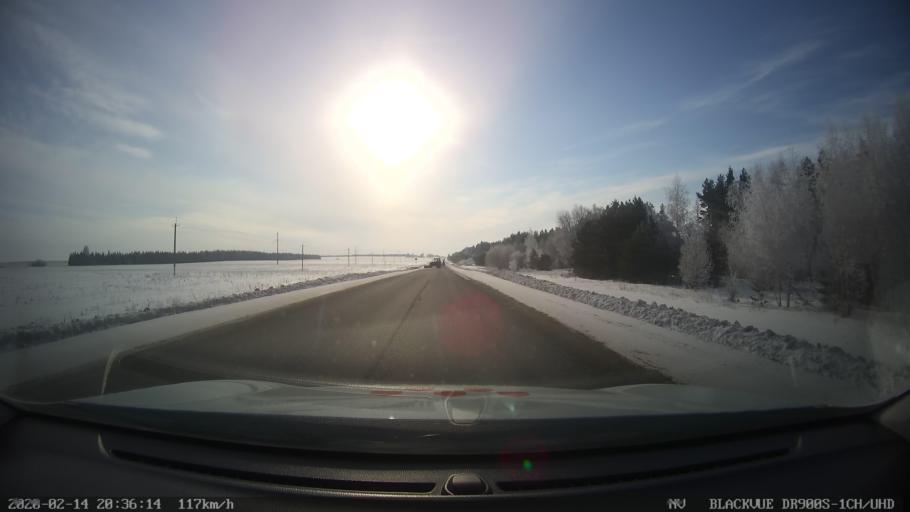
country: RU
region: Tatarstan
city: Kuybyshevskiy Zaton
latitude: 55.3709
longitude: 48.9982
